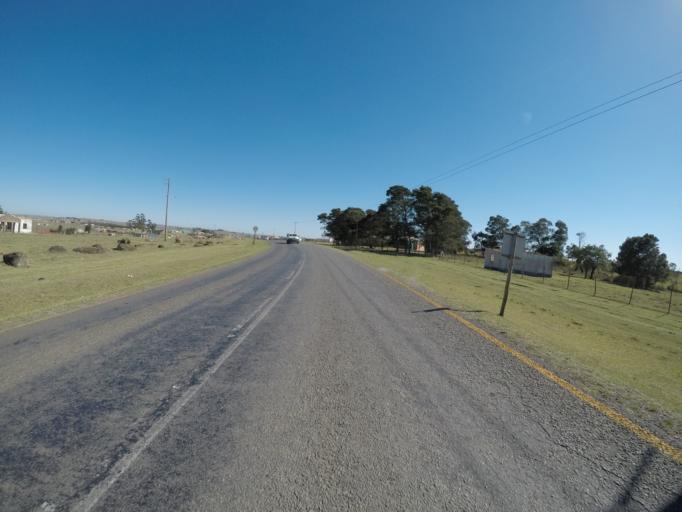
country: ZA
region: Eastern Cape
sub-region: OR Tambo District Municipality
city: Mthatha
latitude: -31.7913
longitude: 28.7452
